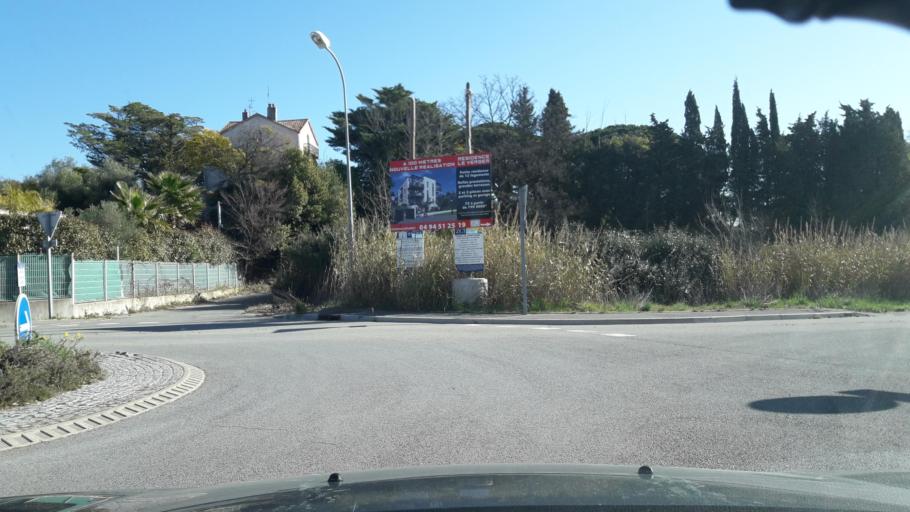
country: FR
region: Provence-Alpes-Cote d'Azur
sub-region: Departement du Var
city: Saint-Raphael
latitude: 43.4421
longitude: 6.7600
